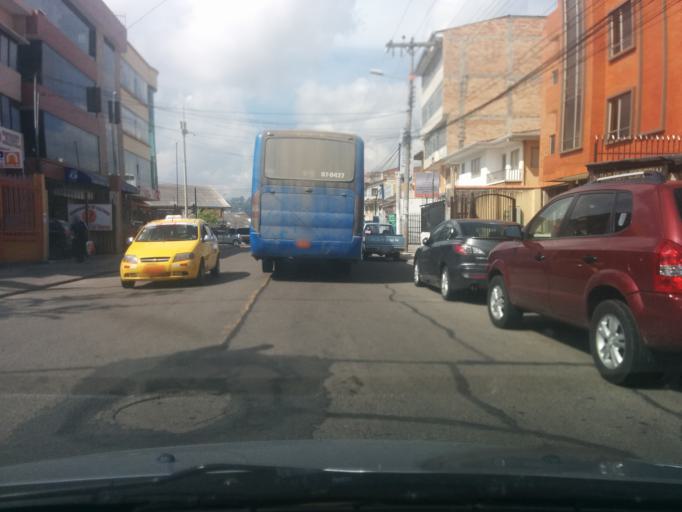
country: EC
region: Azuay
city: Cuenca
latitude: -2.9016
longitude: -78.9922
